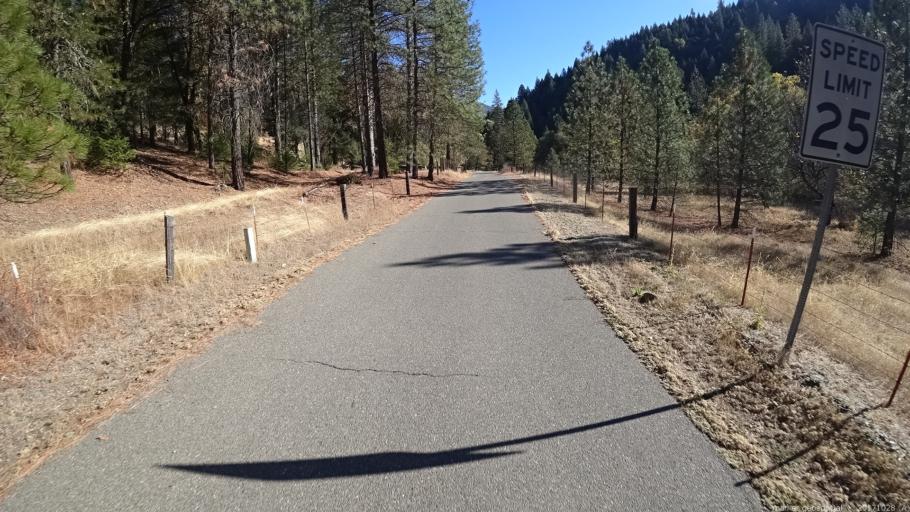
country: US
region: California
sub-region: Shasta County
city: Shasta
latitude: 40.7602
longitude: -122.5720
